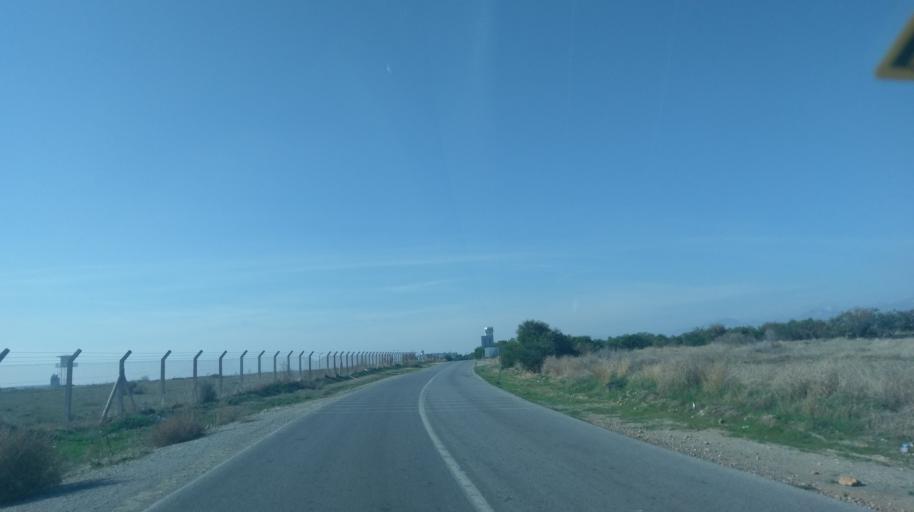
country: CY
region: Larnaka
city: Athienou
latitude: 35.1537
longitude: 33.5158
